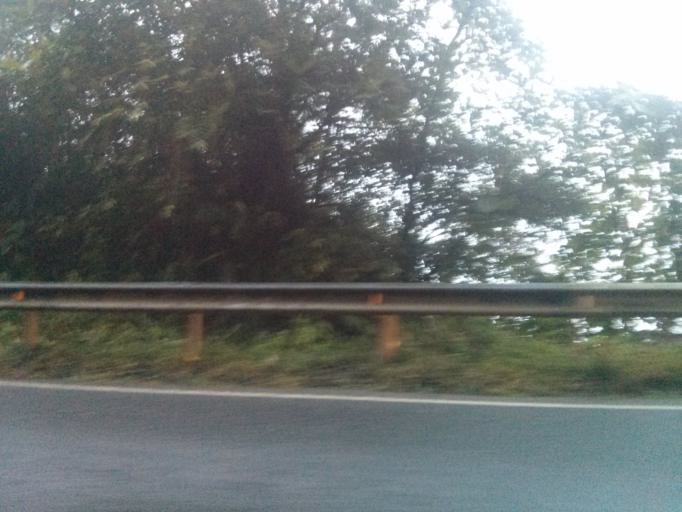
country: CR
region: San Jose
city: Dulce Nombre de Jesus
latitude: 10.0973
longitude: -83.9806
